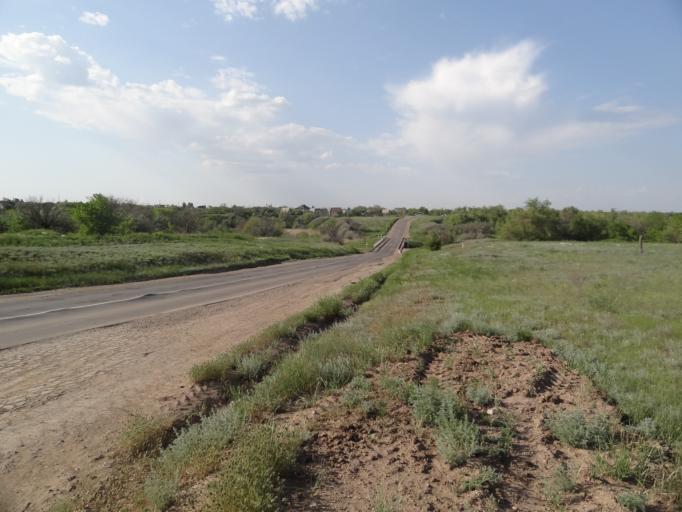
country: RU
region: Saratov
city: Privolzhskiy
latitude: 51.3469
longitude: 46.0445
